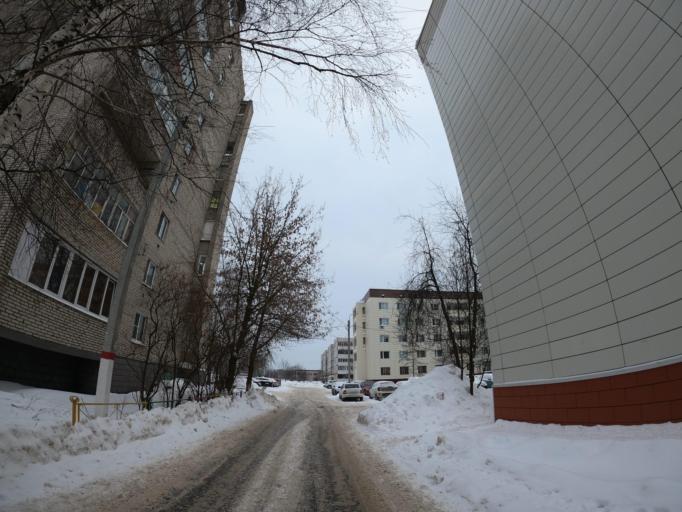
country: RU
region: Moskovskaya
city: Elektrogorsk
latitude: 55.8695
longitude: 38.7815
